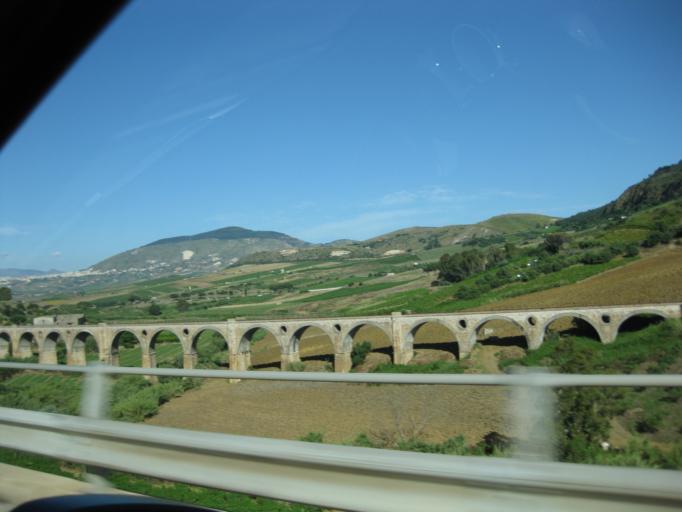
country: IT
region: Sicily
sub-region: Trapani
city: Calatafimi
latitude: 37.9587
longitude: 12.8656
